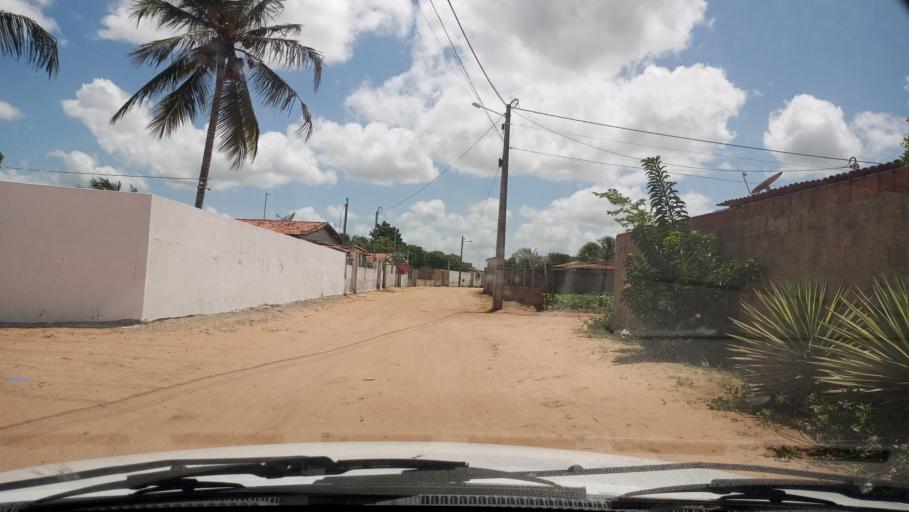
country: BR
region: Rio Grande do Norte
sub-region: Brejinho
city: Brejinho
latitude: -6.2648
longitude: -35.3720
